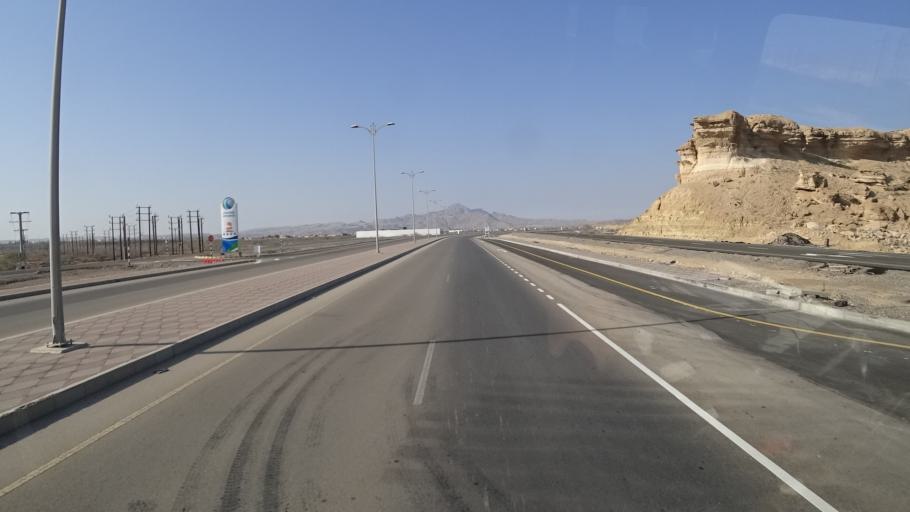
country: OM
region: Ash Sharqiyah
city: Sur
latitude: 22.5921
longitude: 59.4781
